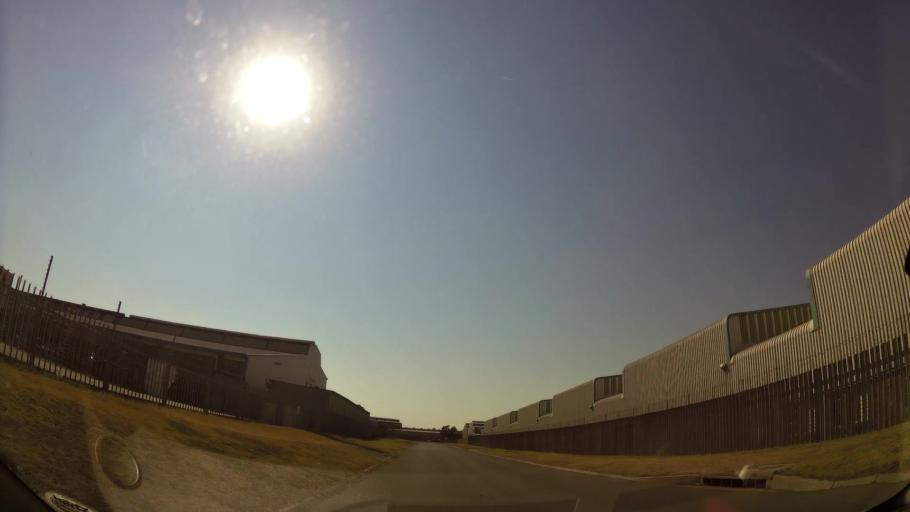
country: ZA
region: Gauteng
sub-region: Ekurhuleni Metropolitan Municipality
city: Boksburg
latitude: -26.1585
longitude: 28.2137
